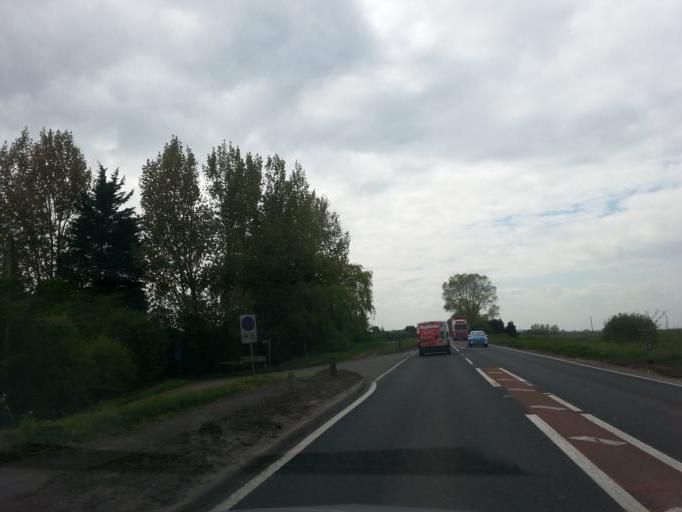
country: GB
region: England
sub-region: Cambridgeshire
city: Wisbech
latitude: 52.6355
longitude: 0.1165
